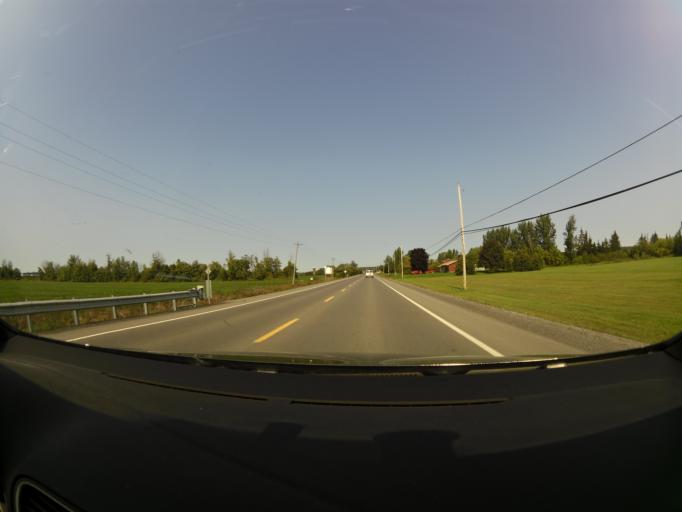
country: CA
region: Ontario
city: Bells Corners
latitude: 45.3252
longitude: -76.0116
